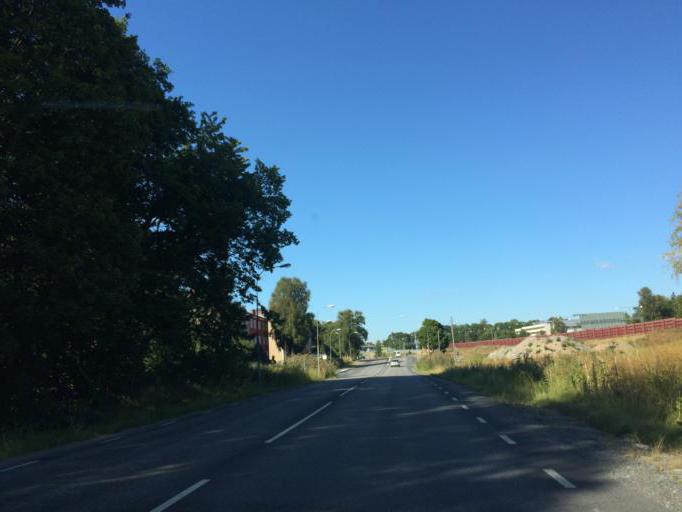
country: SE
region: Stockholm
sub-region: Upplands Vasby Kommun
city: Upplands Vaesby
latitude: 59.4797
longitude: 17.9183
